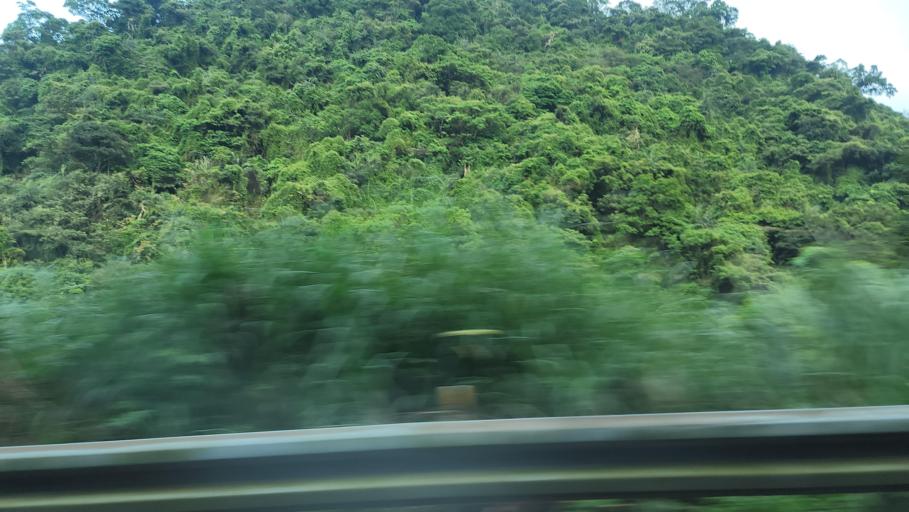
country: TW
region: Taiwan
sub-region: Keelung
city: Keelung
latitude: 25.1627
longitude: 121.6531
